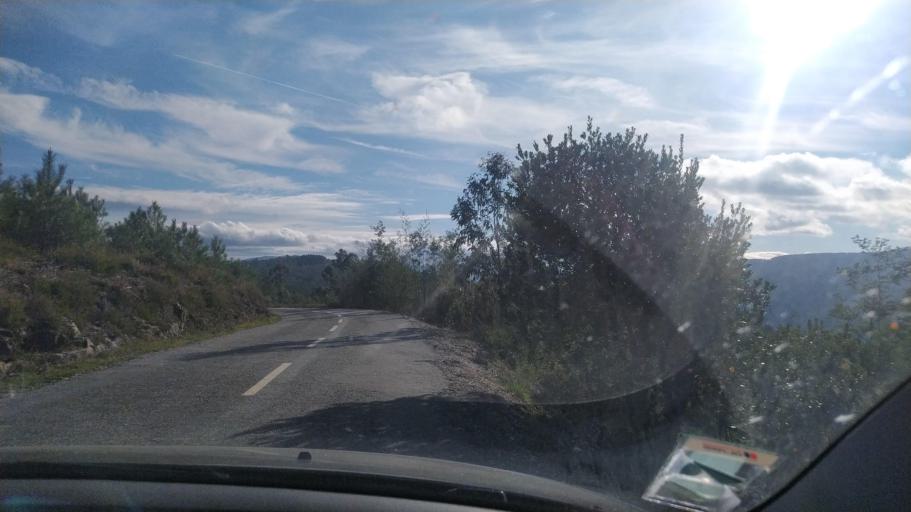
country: PT
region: Castelo Branco
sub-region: Concelho do Fundao
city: Aldeia de Joanes
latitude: 40.1944
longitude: -7.7234
